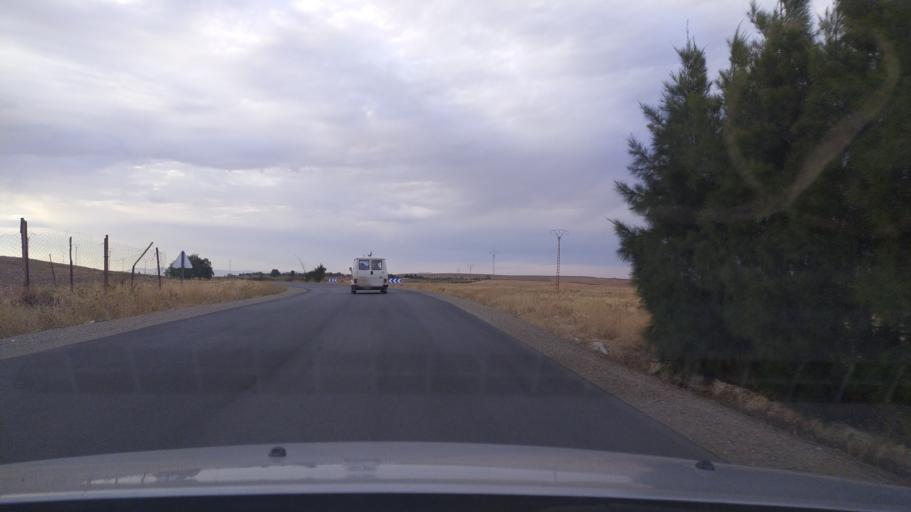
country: DZ
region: Tiaret
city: Frenda
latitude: 35.0131
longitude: 1.1149
